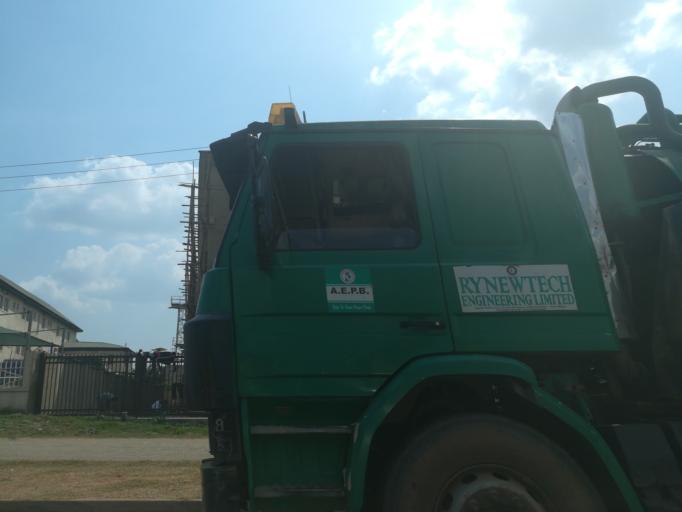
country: NG
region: Abuja Federal Capital Territory
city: Abuja
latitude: 9.0545
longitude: 7.4407
